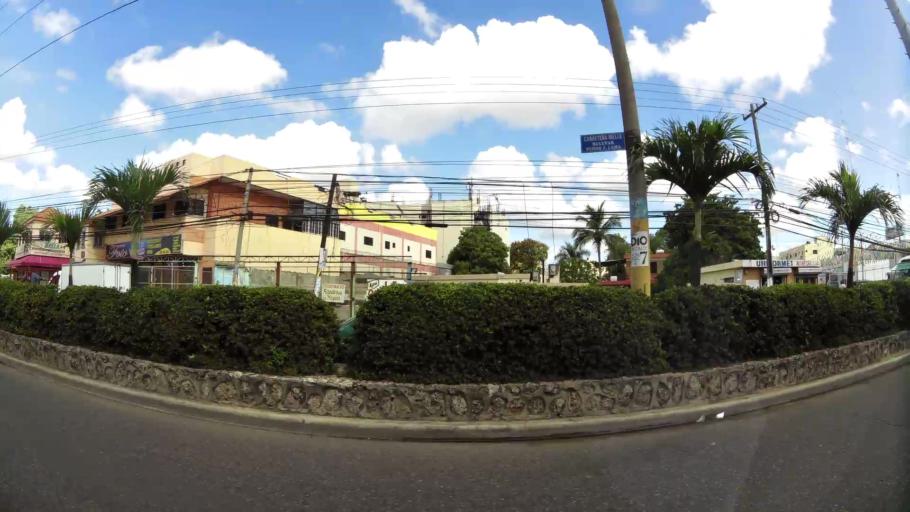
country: DO
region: Santo Domingo
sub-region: Santo Domingo
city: Santo Domingo Este
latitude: 18.5106
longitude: -69.8493
